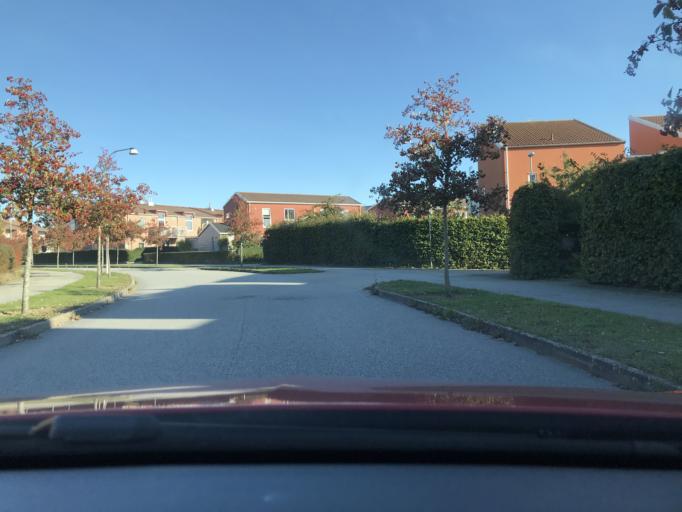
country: SE
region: Skane
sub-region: Lunds Kommun
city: Lund
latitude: 55.7025
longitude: 13.2512
